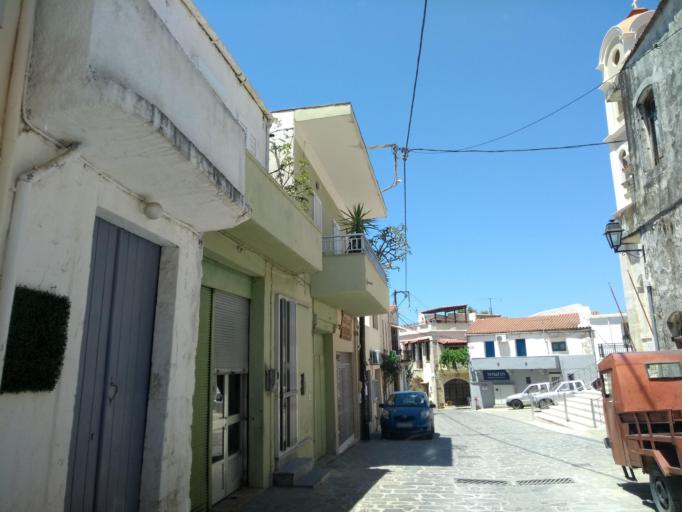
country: GR
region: Crete
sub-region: Nomos Chanias
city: Georgioupolis
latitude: 35.3287
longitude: 24.3356
